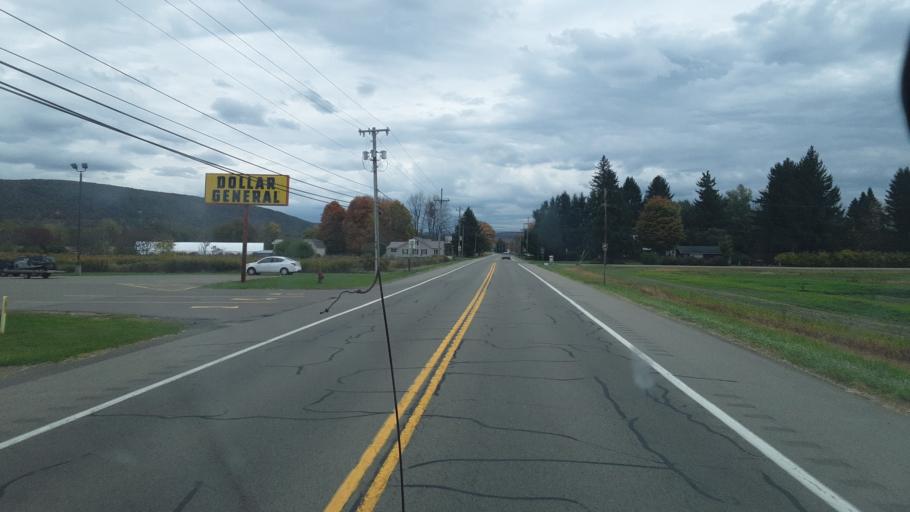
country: US
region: New York
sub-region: Allegany County
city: Belmont
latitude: 42.2096
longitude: -78.0151
